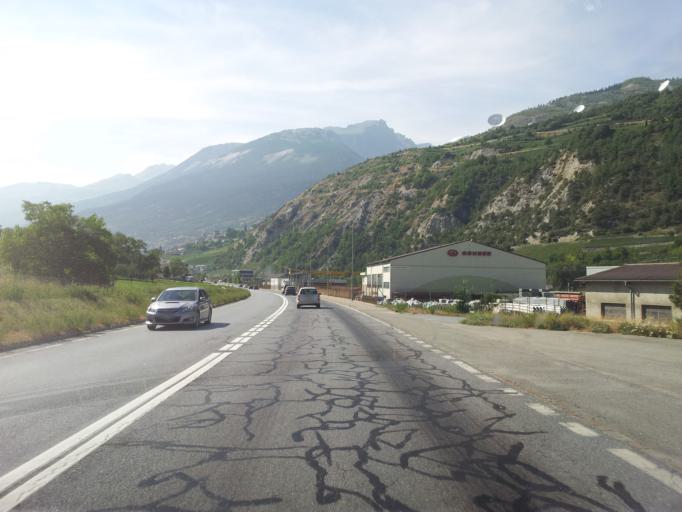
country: CH
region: Valais
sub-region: Leuk District
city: Leuk
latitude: 46.3083
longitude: 7.6518
